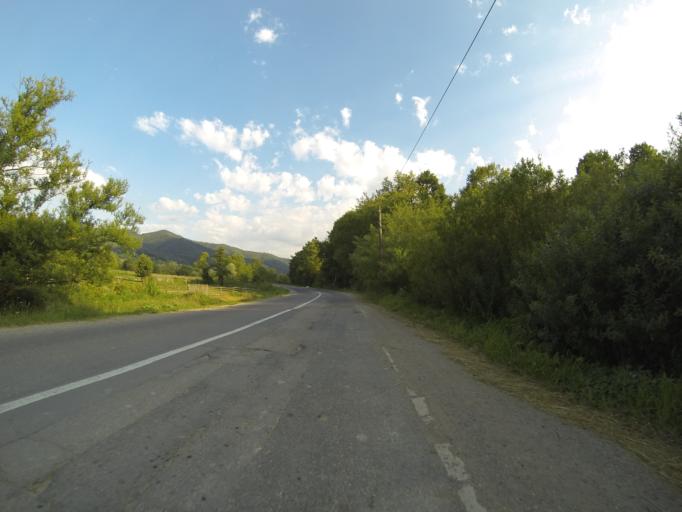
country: RO
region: Brasov
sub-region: Comuna Sinca Noua
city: Sinca Noua
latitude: 45.7146
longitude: 25.2416
